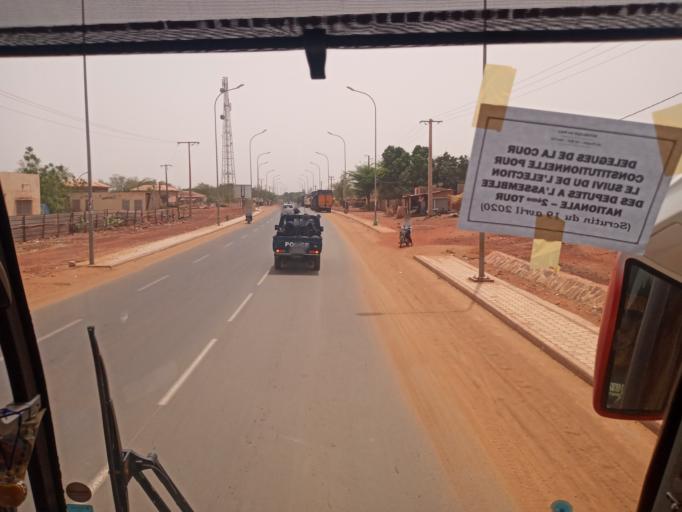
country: ML
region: Koulikoro
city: Koulikoro
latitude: 12.8539
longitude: -7.5662
